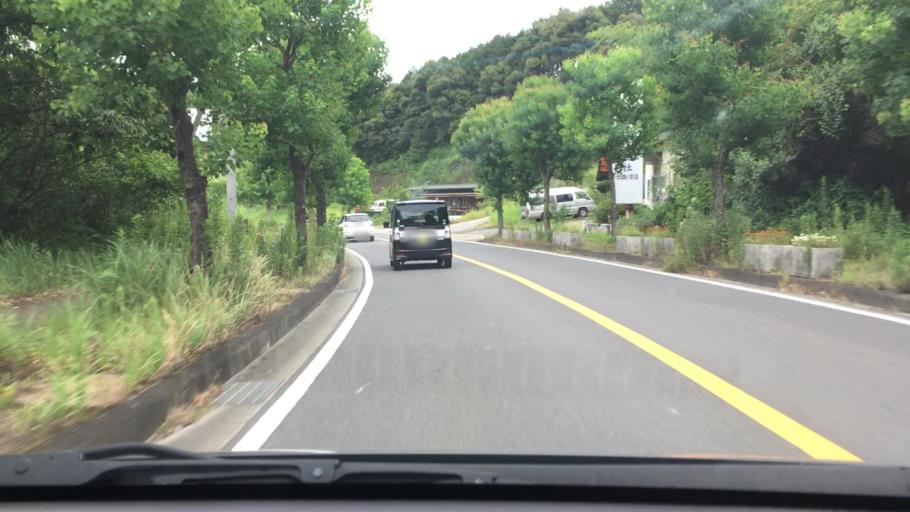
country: JP
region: Nagasaki
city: Togitsu
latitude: 32.9868
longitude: 129.7679
